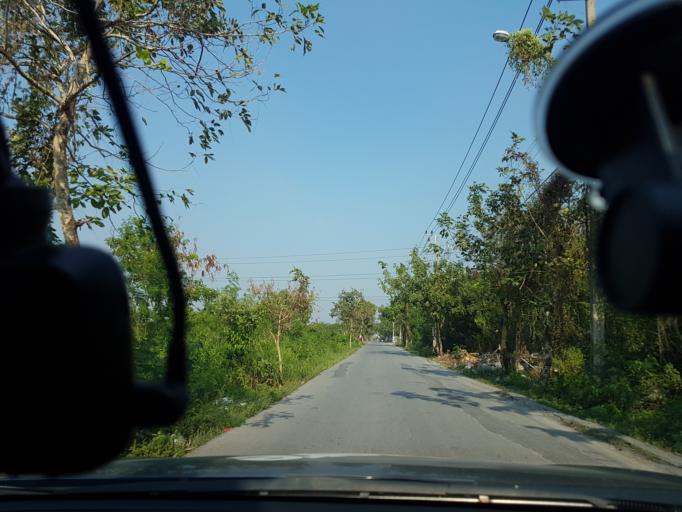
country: TH
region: Pathum Thani
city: Lam Luk Ka
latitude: 13.9105
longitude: 100.7050
